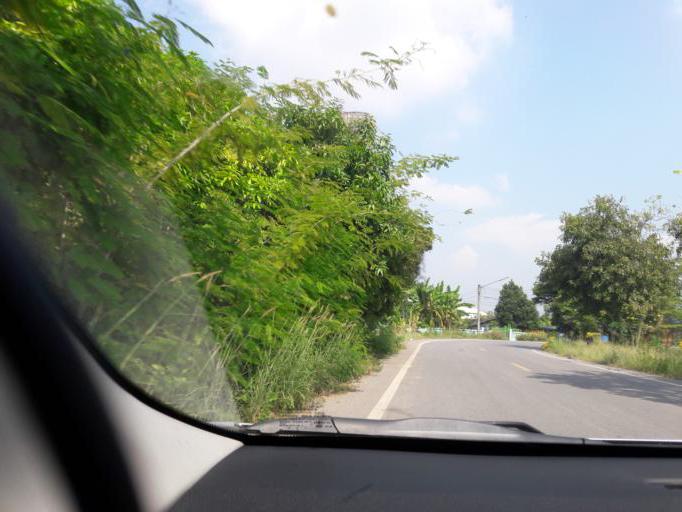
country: TH
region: Ang Thong
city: Ang Thong
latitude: 14.5874
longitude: 100.4320
